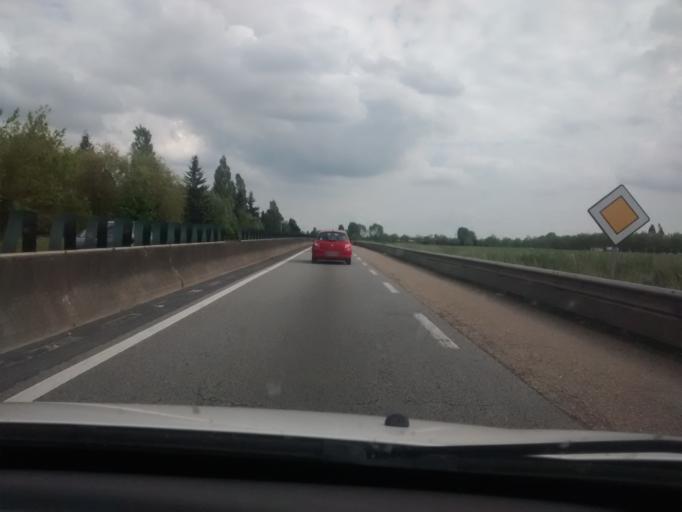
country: FR
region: Ile-de-France
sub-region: Departement des Yvelines
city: Rambouillet
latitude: 48.6600
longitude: 1.8377
